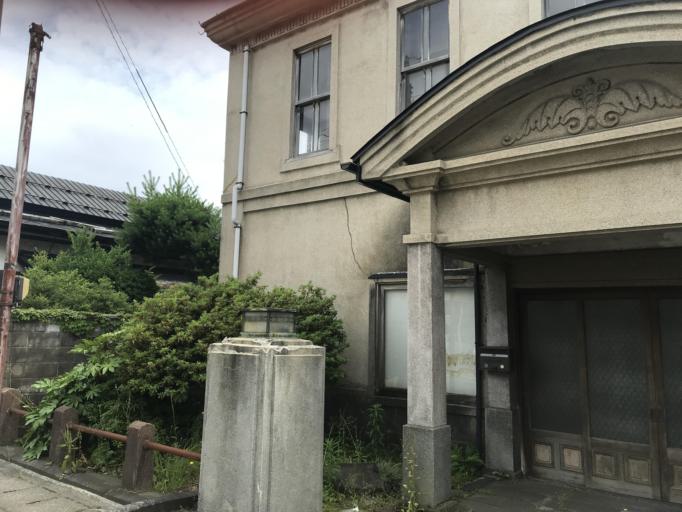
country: JP
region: Akita
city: Tenno
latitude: 39.8840
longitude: 139.8471
